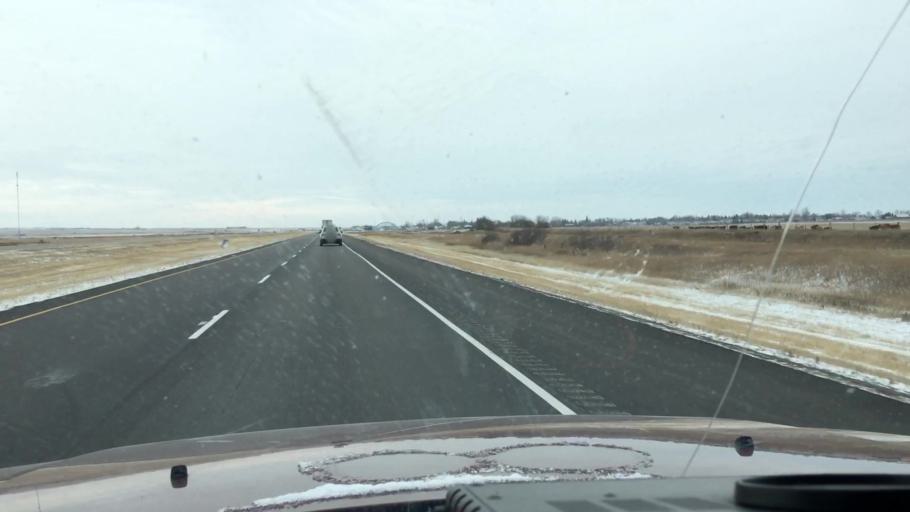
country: CA
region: Saskatchewan
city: Saskatoon
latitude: 51.8256
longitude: -106.5007
